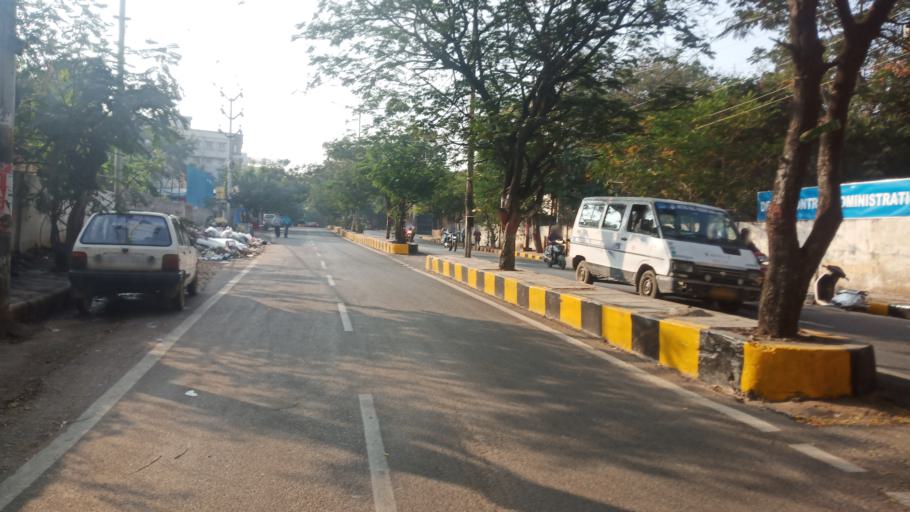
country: IN
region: Telangana
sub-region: Rangareddi
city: Kukatpalli
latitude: 17.4428
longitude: 78.4382
